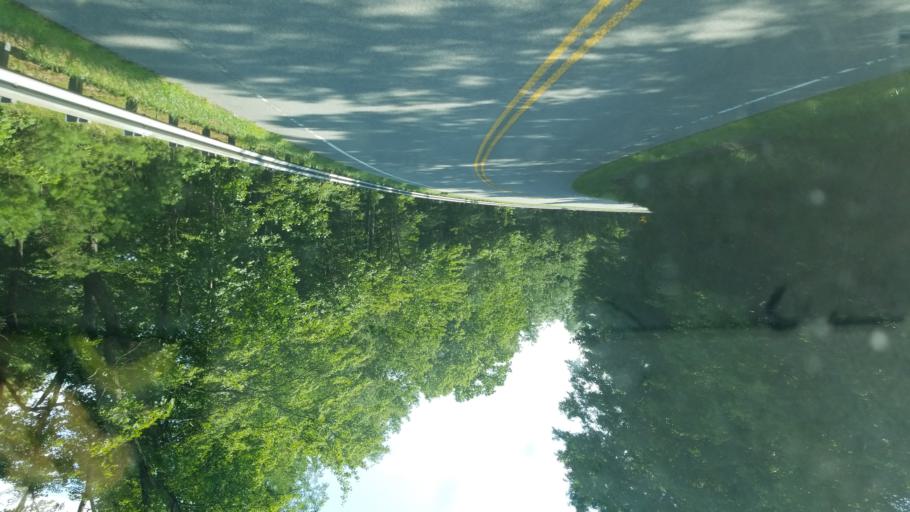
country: US
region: North Carolina
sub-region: Avery County
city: Newland
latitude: 35.9298
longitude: -81.8214
